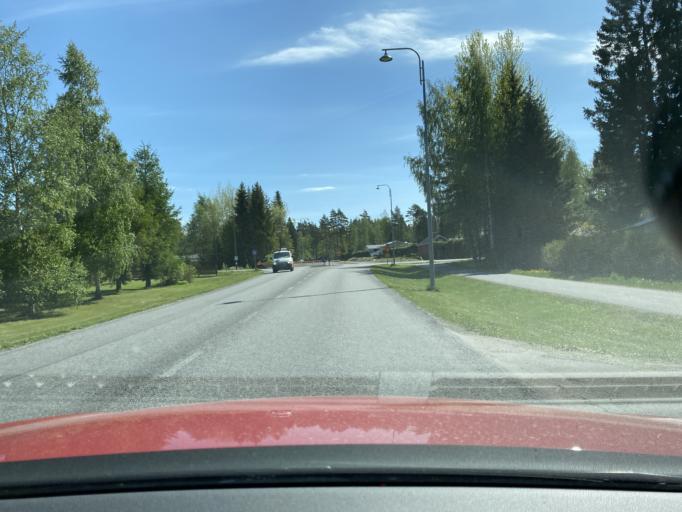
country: FI
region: Satakunta
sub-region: Rauma
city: Eura
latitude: 61.1236
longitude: 22.1588
